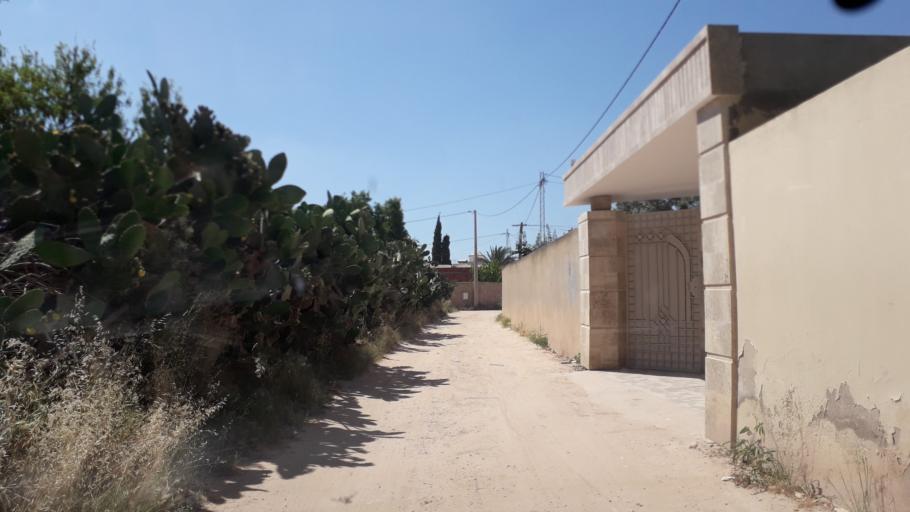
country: TN
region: Safaqis
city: Al Qarmadah
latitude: 34.8179
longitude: 10.7645
